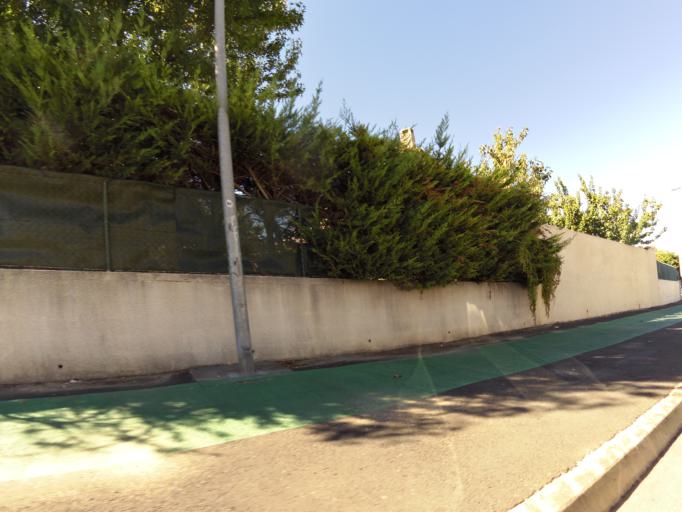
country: FR
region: Languedoc-Roussillon
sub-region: Departement de l'Herault
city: Lunel
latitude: 43.6683
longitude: 4.1342
